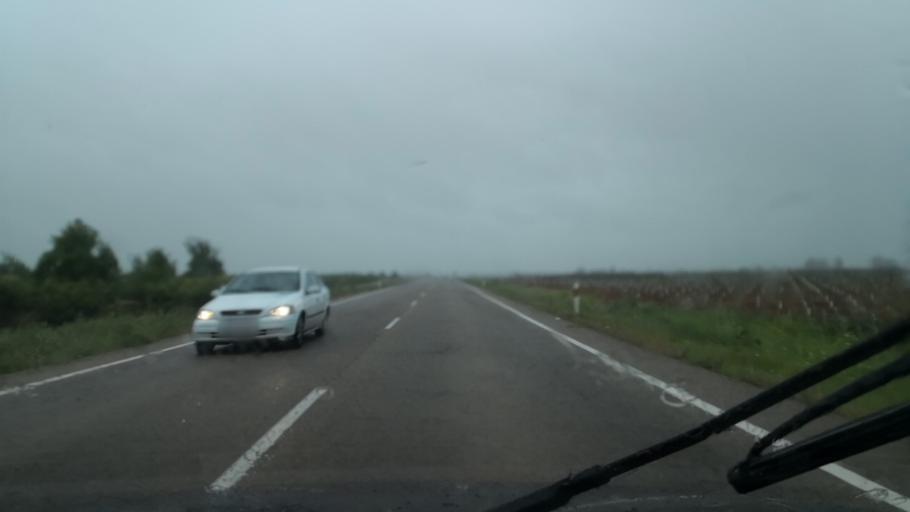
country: ES
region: Extremadura
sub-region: Provincia de Badajoz
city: Badajoz
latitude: 38.9375
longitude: -6.9223
